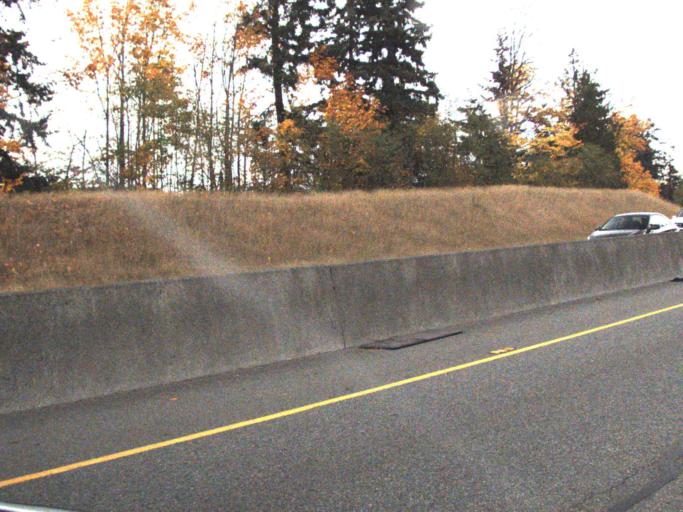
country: US
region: Washington
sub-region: Snohomish County
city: Alderwood Manor
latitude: 47.8565
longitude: -122.2745
